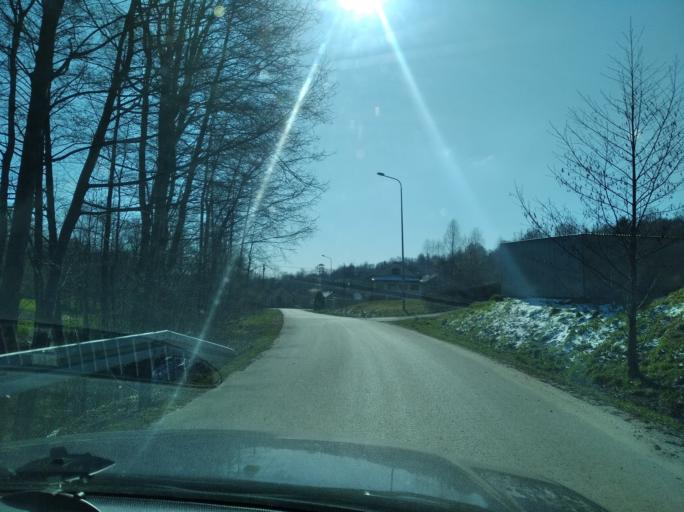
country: PL
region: Subcarpathian Voivodeship
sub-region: Powiat strzyzowski
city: Jawornik
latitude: 49.8492
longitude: 21.8722
